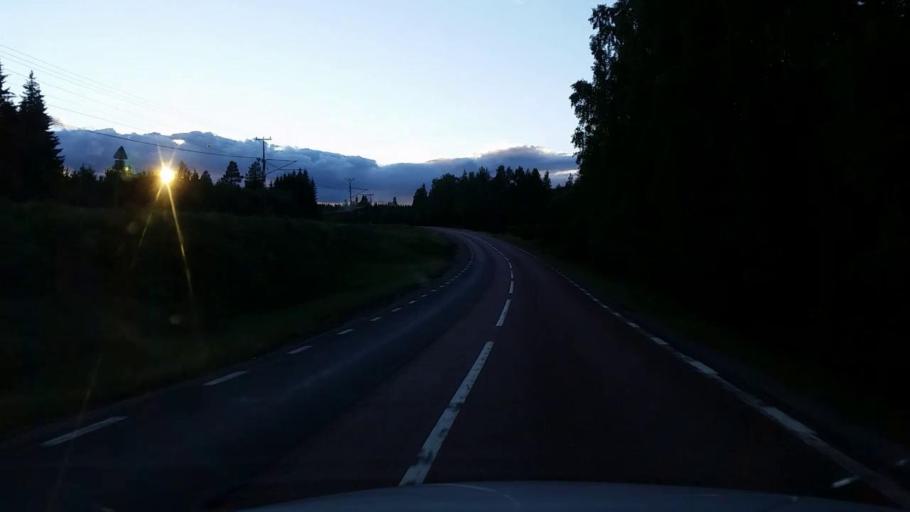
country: SE
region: Gaevleborg
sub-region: Ljusdals Kommun
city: Farila
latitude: 62.0834
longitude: 15.8148
